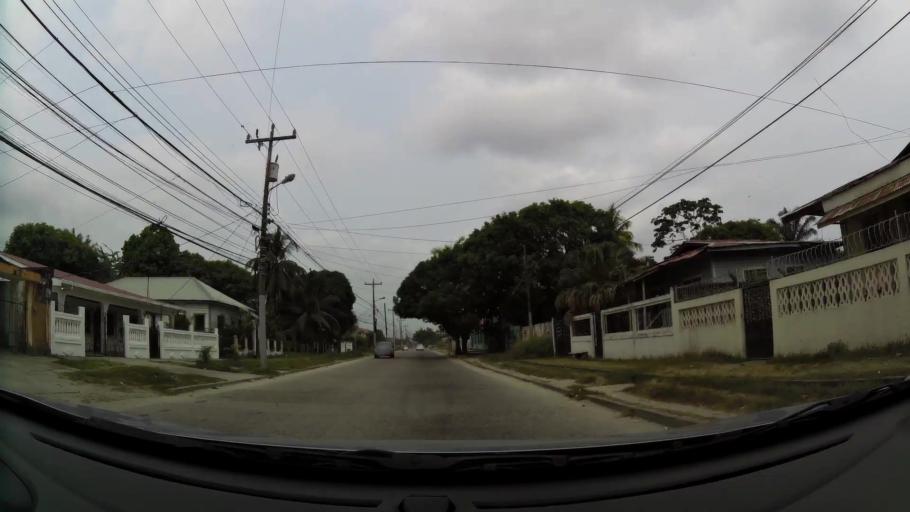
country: HN
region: Atlantida
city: Tela
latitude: 15.7779
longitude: -87.4657
